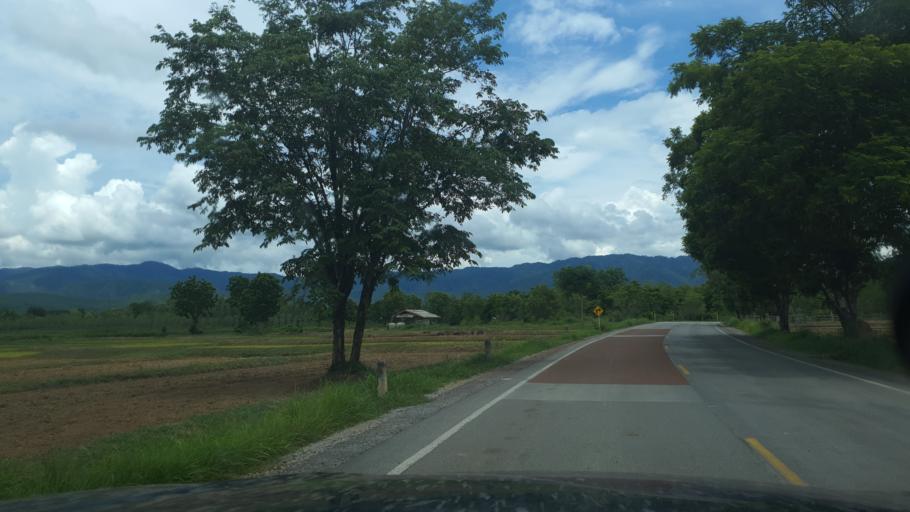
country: TH
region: Lampang
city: Sop Prap
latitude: 17.9193
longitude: 99.3868
